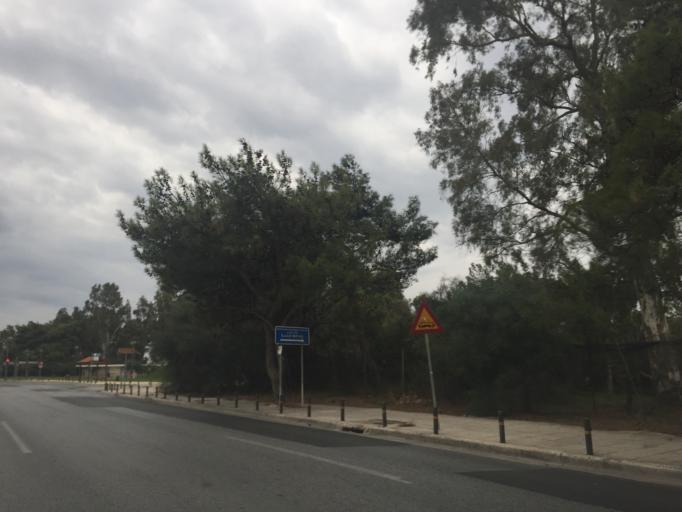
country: GR
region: Attica
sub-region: Nomarchia Athinas
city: Glyfada
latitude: 37.8546
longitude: 23.7517
